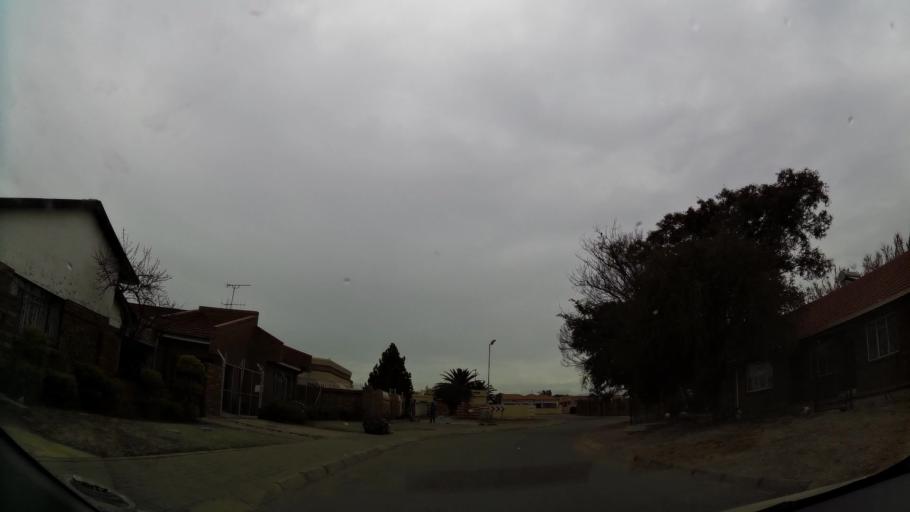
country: ZA
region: Gauteng
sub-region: City of Tshwane Metropolitan Municipality
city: Pretoria
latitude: -25.7121
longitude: 28.3415
